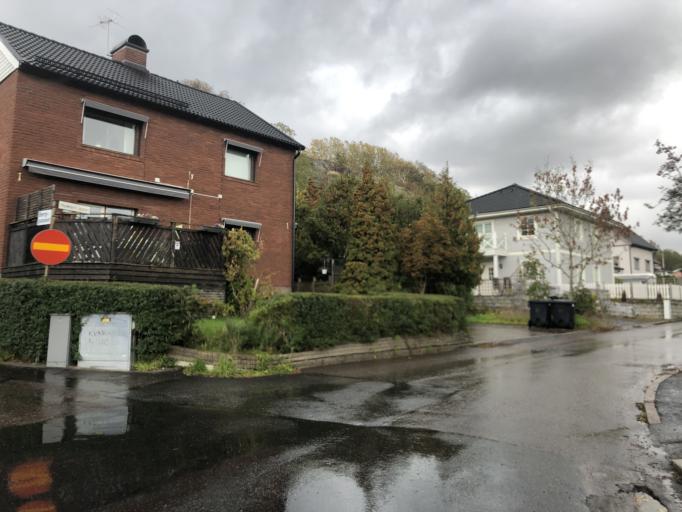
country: SE
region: Vaestra Goetaland
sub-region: Molndal
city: Moelndal
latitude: 57.6512
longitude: 12.0323
